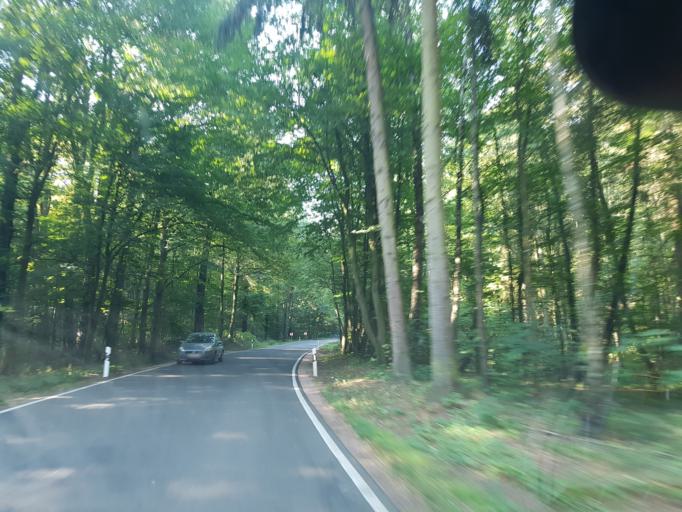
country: DE
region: Saxony
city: Waldheim
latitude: 51.0757
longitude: 13.0439
